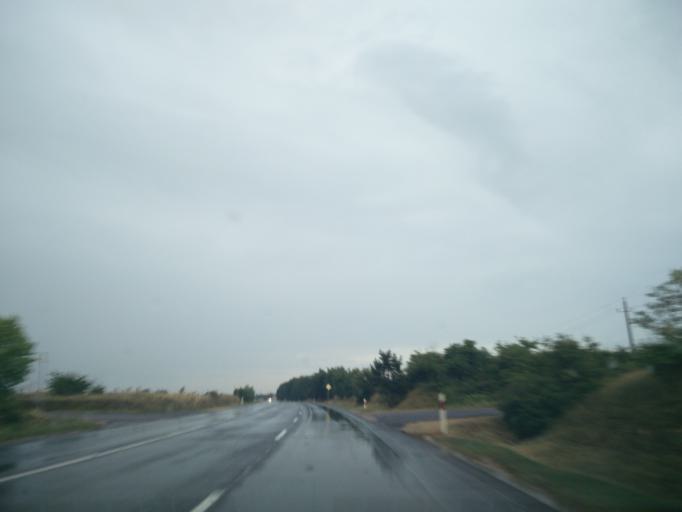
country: HU
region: Veszprem
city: Veszprem
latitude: 47.0880
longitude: 17.8801
